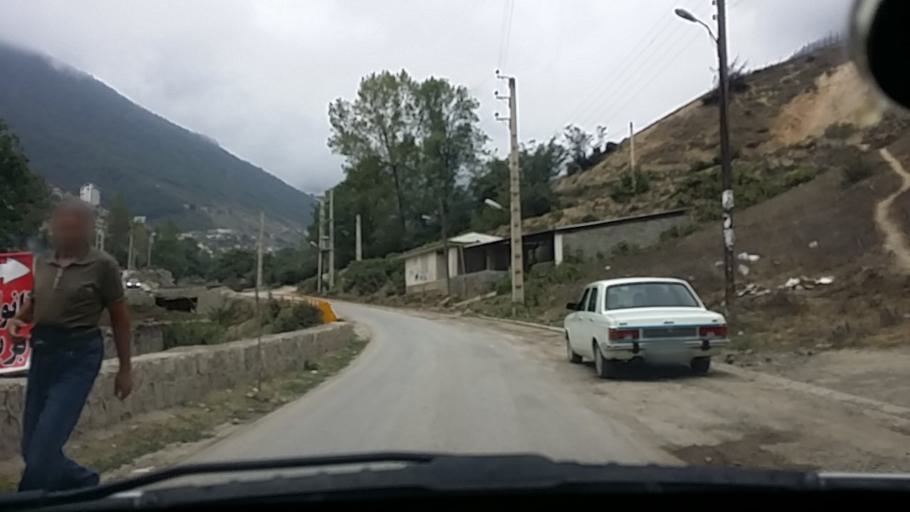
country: IR
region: Mazandaran
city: `Abbasabad
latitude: 36.4816
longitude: 51.1372
